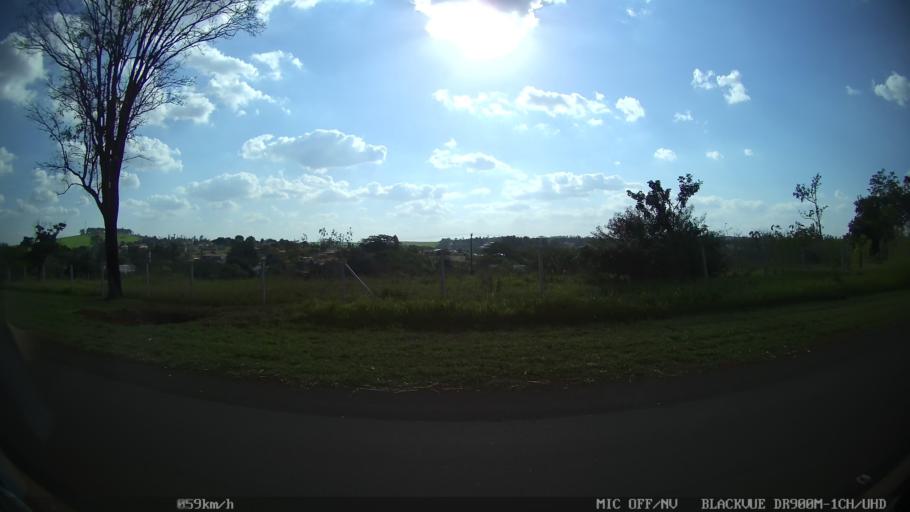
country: BR
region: Sao Paulo
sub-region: Ribeirao Preto
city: Ribeirao Preto
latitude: -21.1825
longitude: -47.8590
